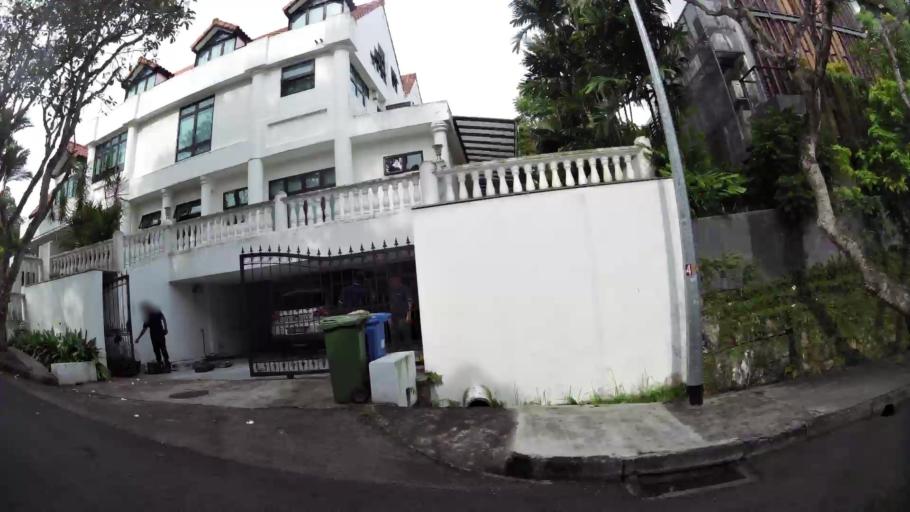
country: SG
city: Singapore
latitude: 1.3201
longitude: 103.7942
